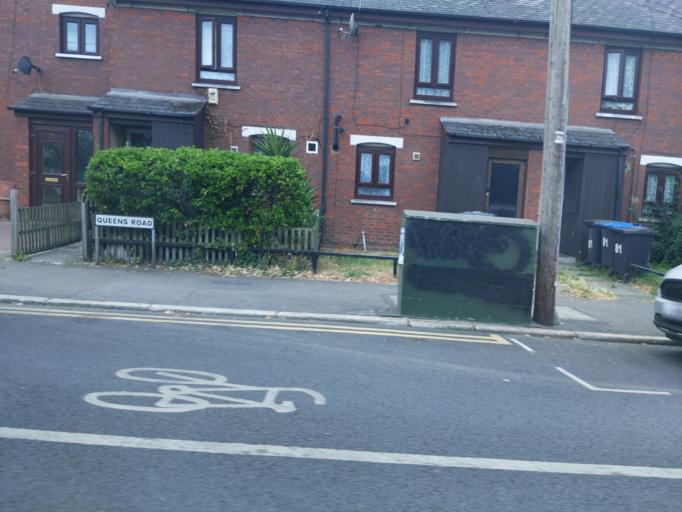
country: GB
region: England
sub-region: Greater London
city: Croydon
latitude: 51.3876
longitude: -0.1025
